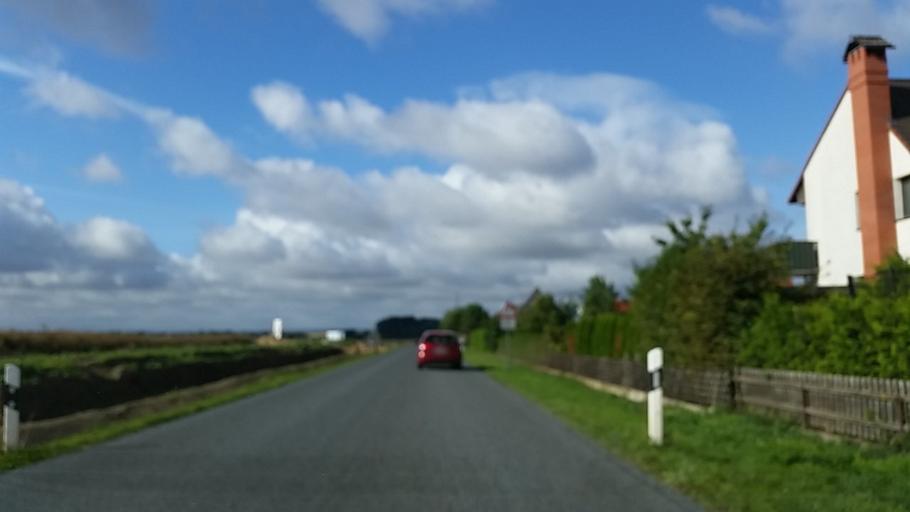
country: DE
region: Lower Saxony
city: Sickte
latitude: 52.2099
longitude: 10.6341
